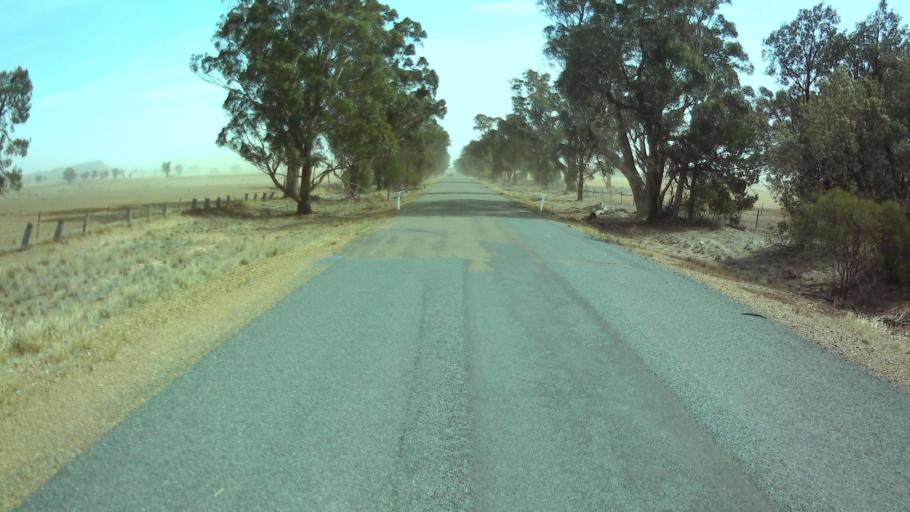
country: AU
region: New South Wales
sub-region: Weddin
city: Grenfell
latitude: -33.7610
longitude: 147.9888
